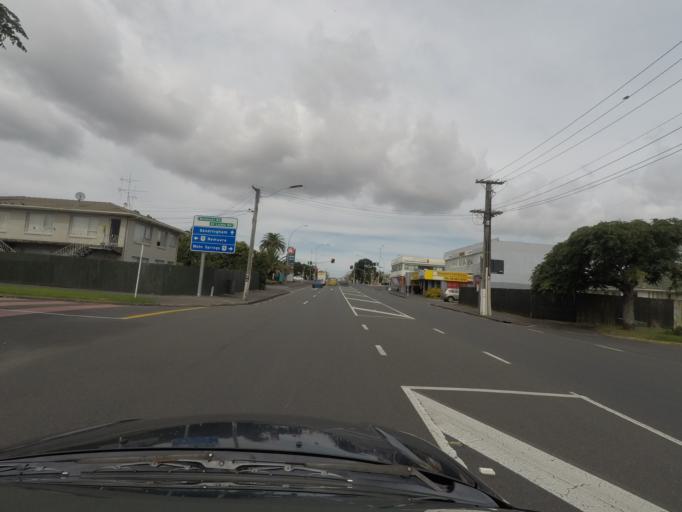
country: NZ
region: Auckland
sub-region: Auckland
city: Auckland
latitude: -36.8841
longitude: 174.7388
